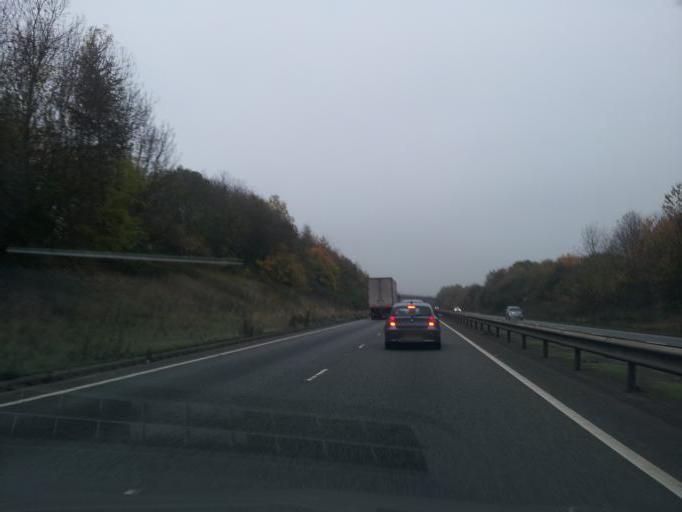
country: GB
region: England
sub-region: Leicestershire
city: Anstey
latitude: 52.6789
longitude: -1.1715
